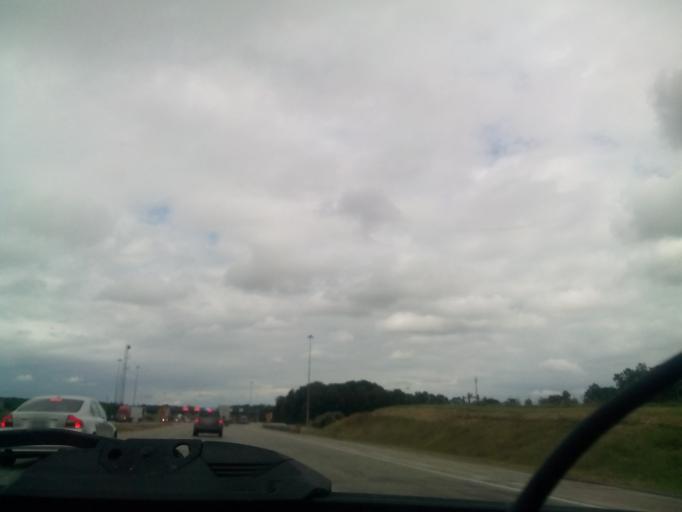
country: US
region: Ohio
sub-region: Williams County
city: Montpelier
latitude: 41.6293
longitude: -84.7587
